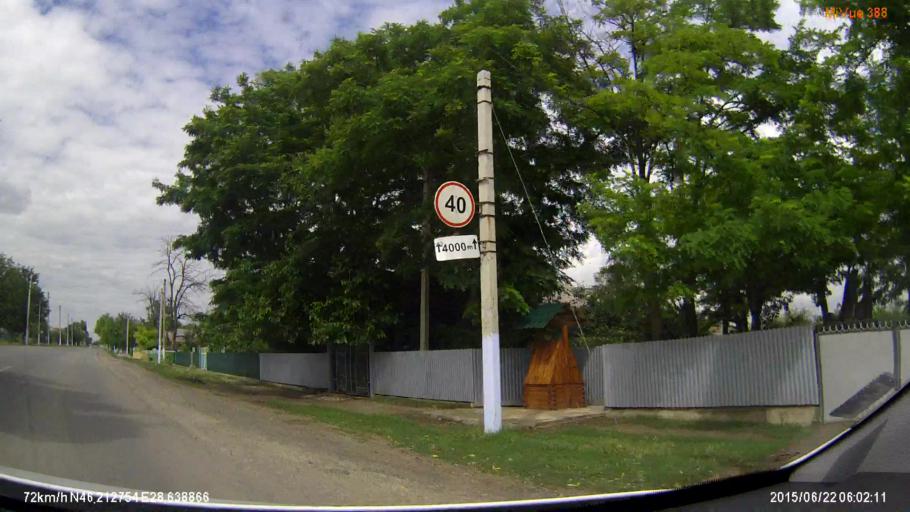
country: MD
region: Gagauzia
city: Comrat
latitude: 46.2124
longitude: 28.6387
